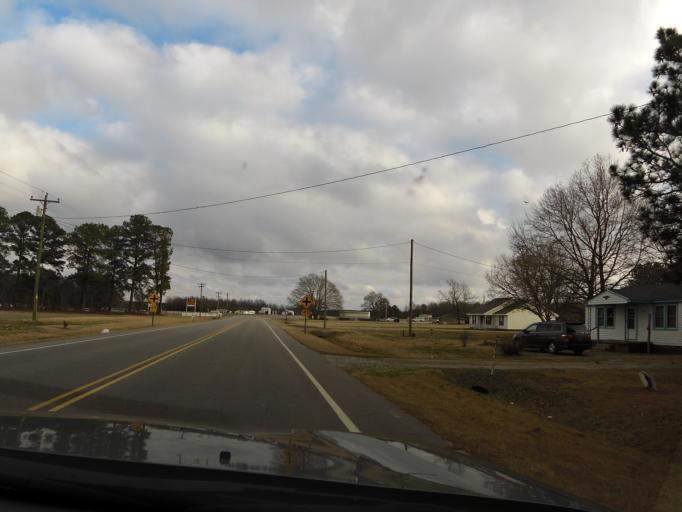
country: US
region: North Carolina
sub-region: Edgecombe County
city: Pinetops
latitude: 35.8111
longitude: -77.6524
